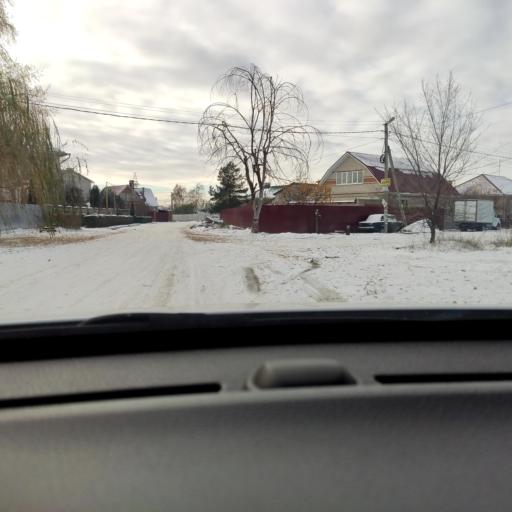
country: RU
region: Voronezj
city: Maslovka
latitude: 51.6309
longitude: 39.2773
